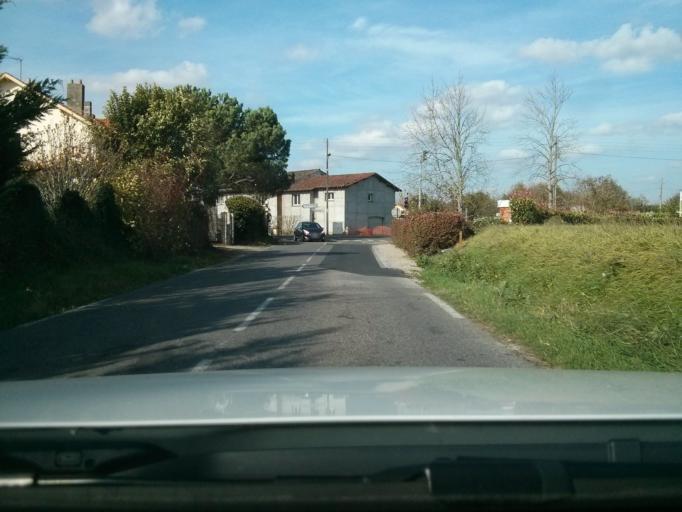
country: FR
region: Midi-Pyrenees
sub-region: Departement du Tarn-et-Garonne
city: Montbeton
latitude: 44.0172
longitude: 1.3207
